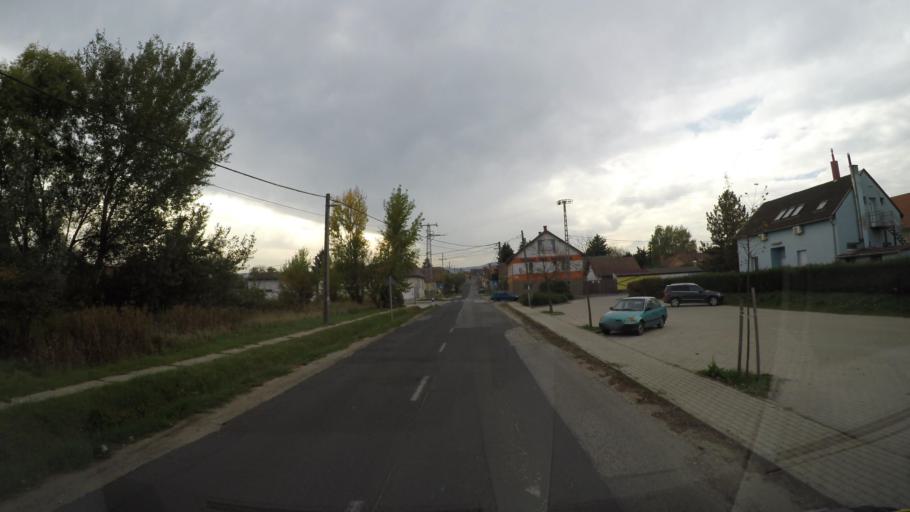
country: HU
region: Pest
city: Pilisvorosvar
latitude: 47.6244
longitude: 18.9137
